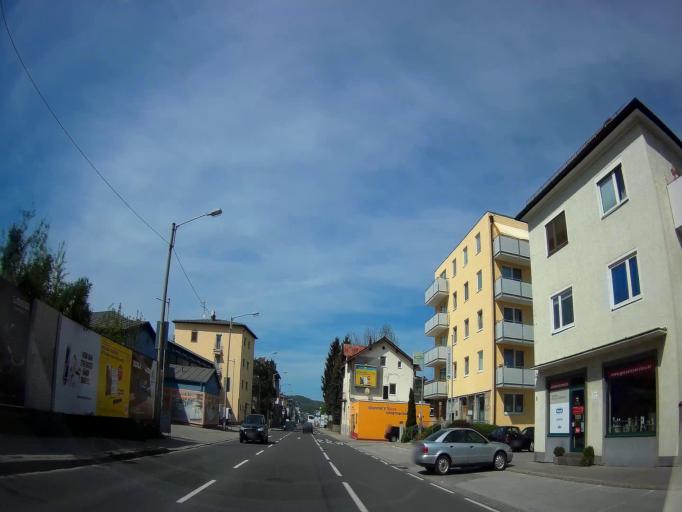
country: AT
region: Salzburg
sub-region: Salzburg Stadt
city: Salzburg
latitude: 47.8107
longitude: 13.0547
